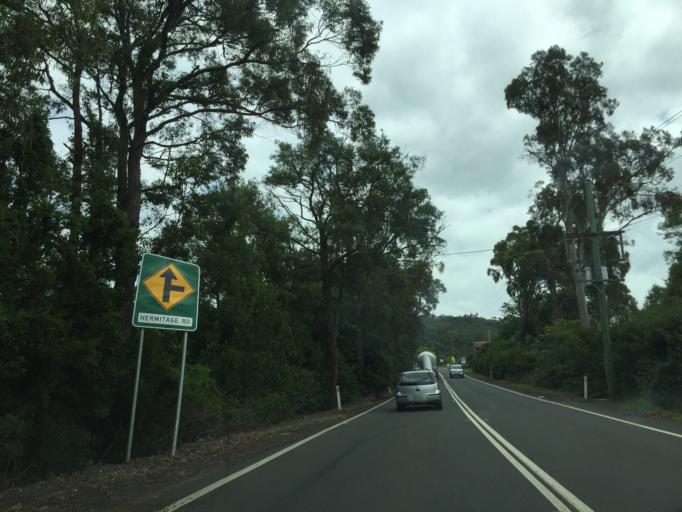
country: AU
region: New South Wales
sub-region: Hawkesbury
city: Richmond
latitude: -33.5439
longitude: 150.6464
